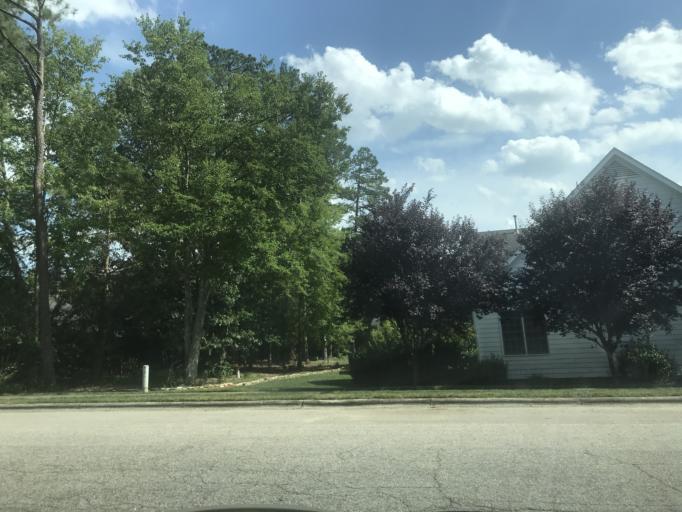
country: US
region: North Carolina
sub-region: Wake County
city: West Raleigh
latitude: 35.8677
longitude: -78.7088
